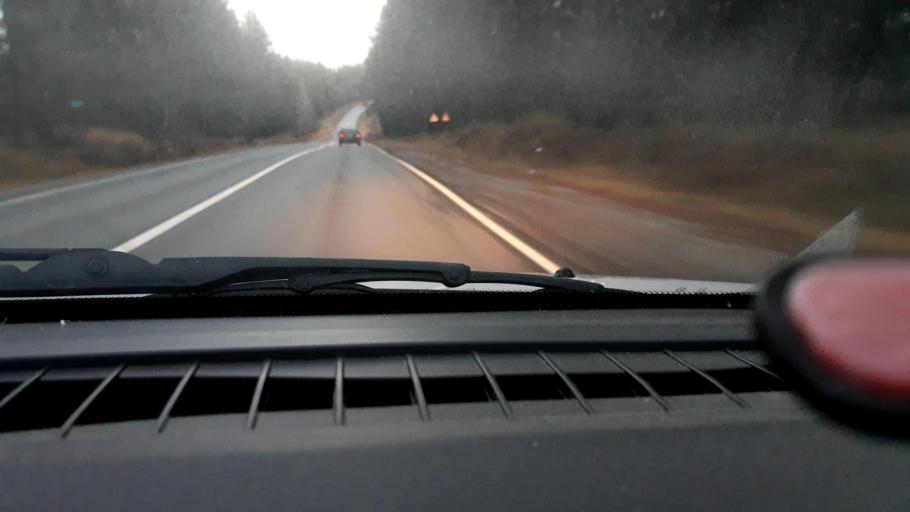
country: RU
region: Nizjnij Novgorod
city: Krasnyye Baki
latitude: 56.9912
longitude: 45.1156
